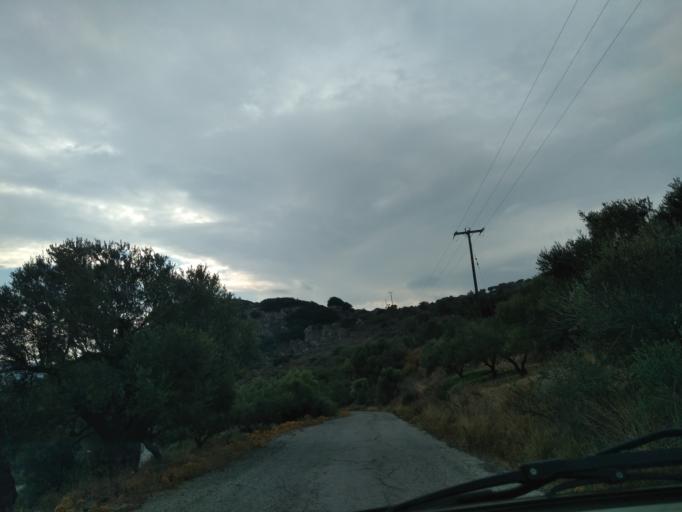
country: GR
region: Crete
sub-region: Nomos Lasithiou
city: Makry-Gialos
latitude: 35.1258
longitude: 26.0221
